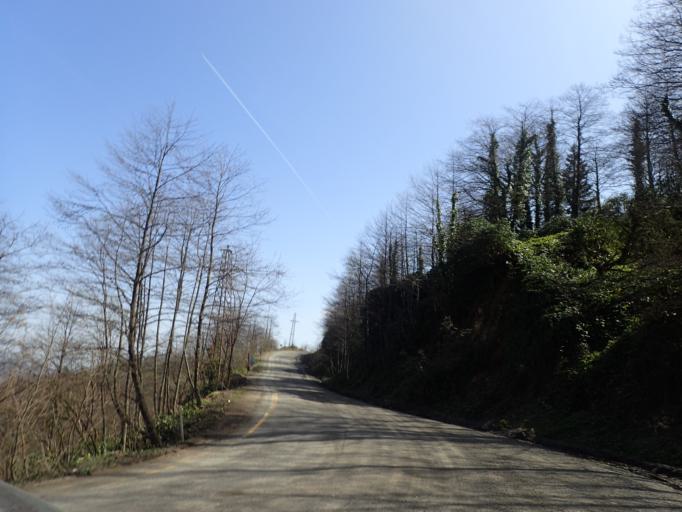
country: TR
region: Ordu
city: Kabaduz
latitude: 40.8239
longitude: 37.9004
